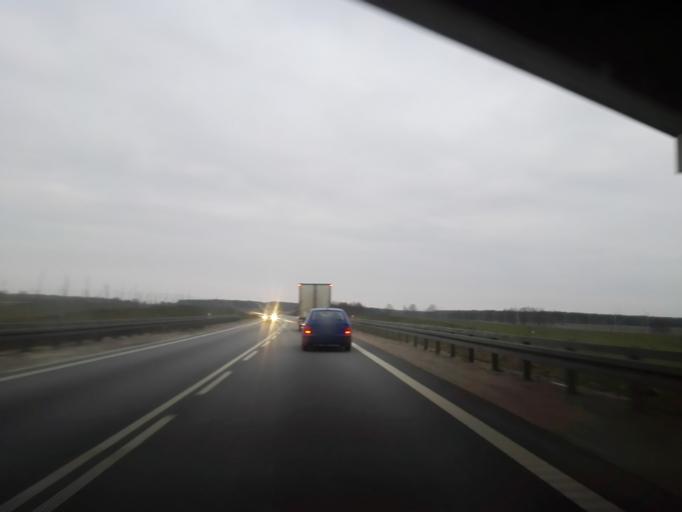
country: PL
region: Podlasie
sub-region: Powiat kolnenski
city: Stawiski
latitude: 53.3731
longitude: 22.1462
